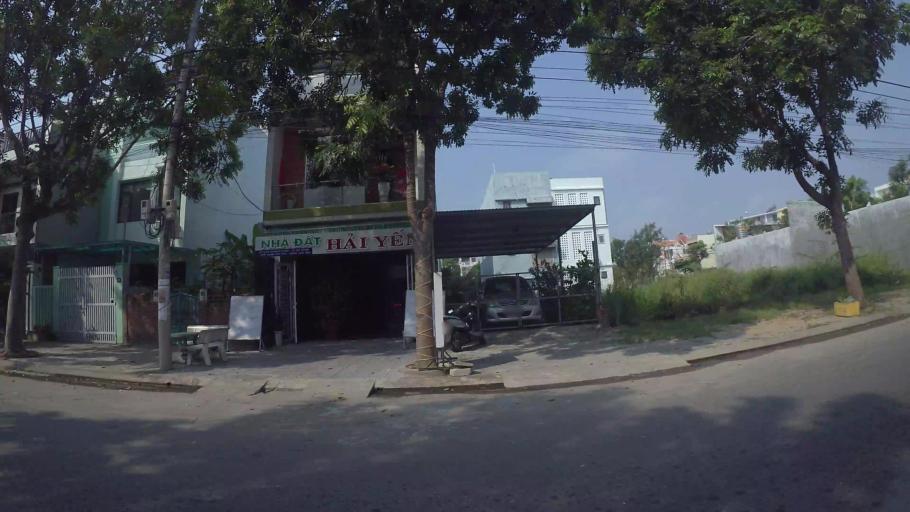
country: VN
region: Da Nang
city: Ngu Hanh Son
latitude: 16.0313
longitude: 108.2411
